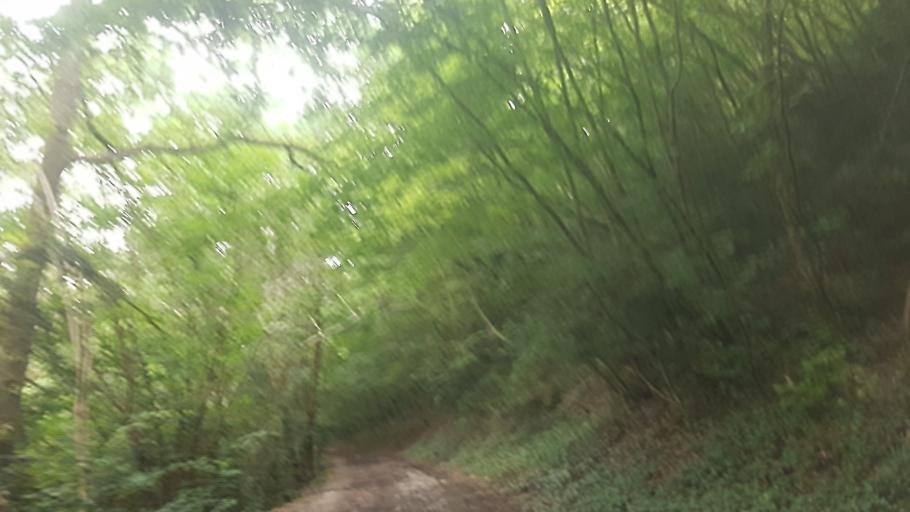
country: BE
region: Wallonia
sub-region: Province de Namur
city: Couvin
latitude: 50.0885
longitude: 4.5530
